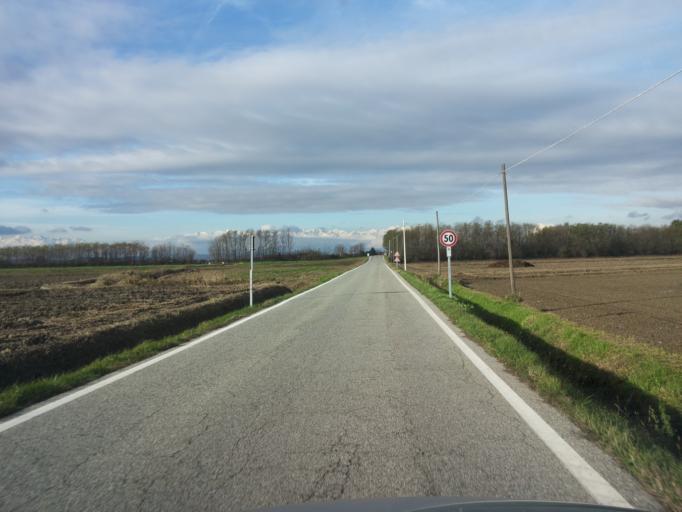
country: IT
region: Piedmont
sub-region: Provincia di Vercelli
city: Crova
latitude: 45.3193
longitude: 8.1962
